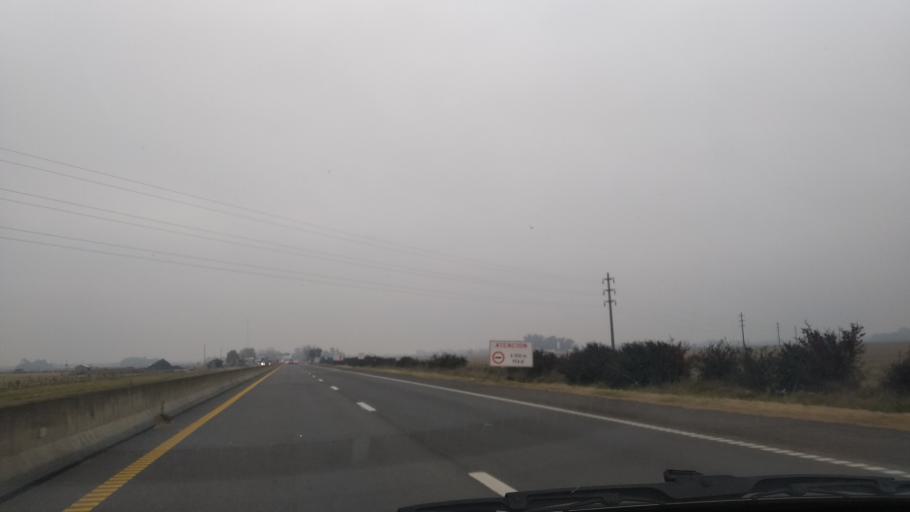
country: AR
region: Buenos Aires
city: Olavarria
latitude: -36.8585
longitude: -60.1188
